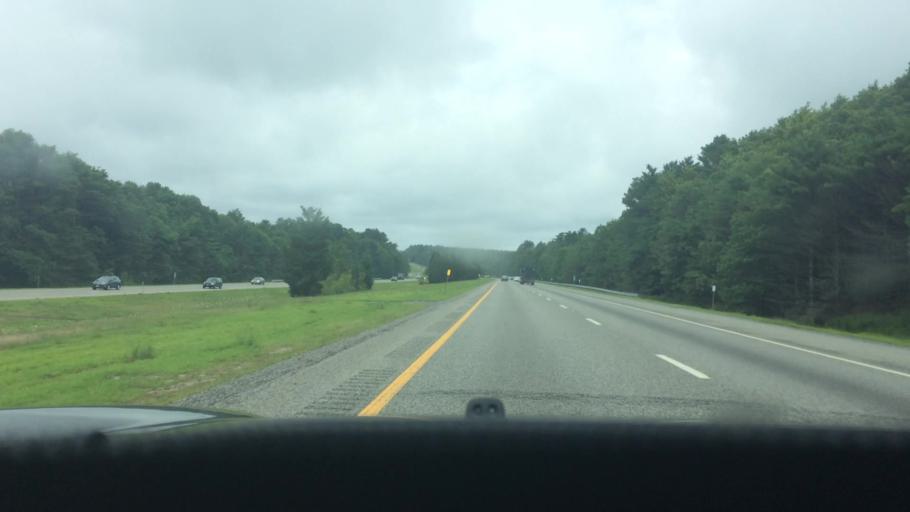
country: US
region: Rhode Island
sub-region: Kent County
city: West Greenwich
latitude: 41.6343
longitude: -71.6306
